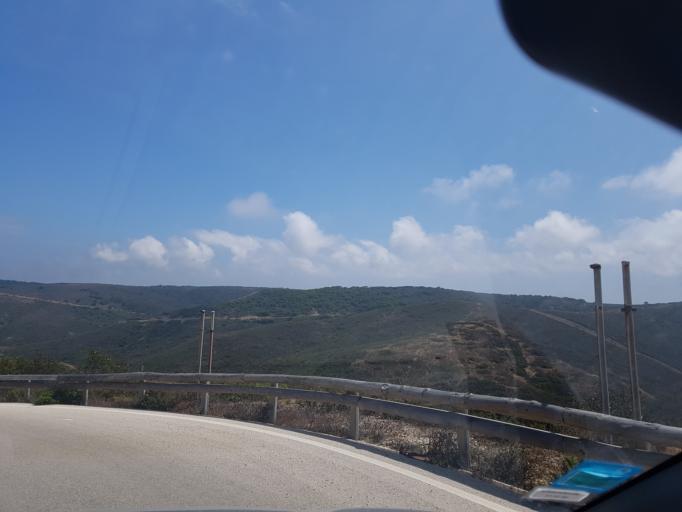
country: PT
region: Faro
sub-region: Vila do Bispo
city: Vila do Bispo
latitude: 37.0987
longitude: -8.9366
